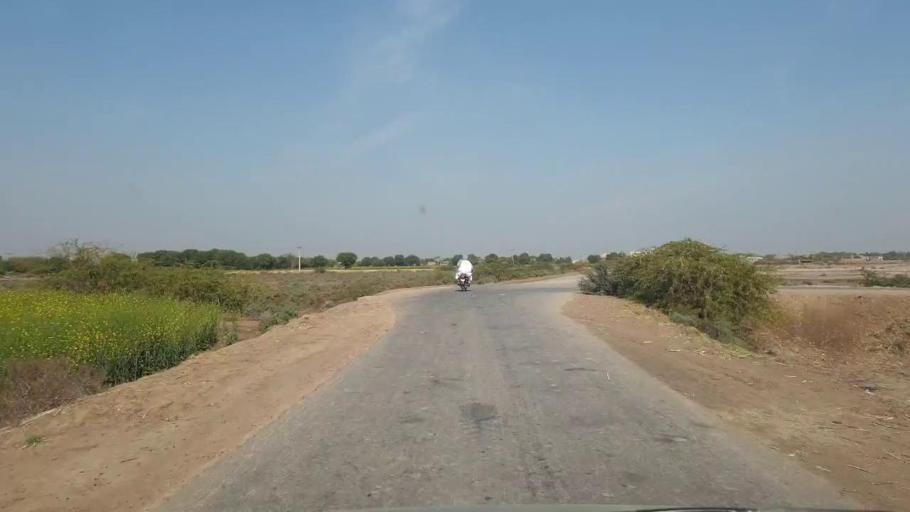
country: PK
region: Sindh
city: Chambar
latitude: 25.3232
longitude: 68.8218
